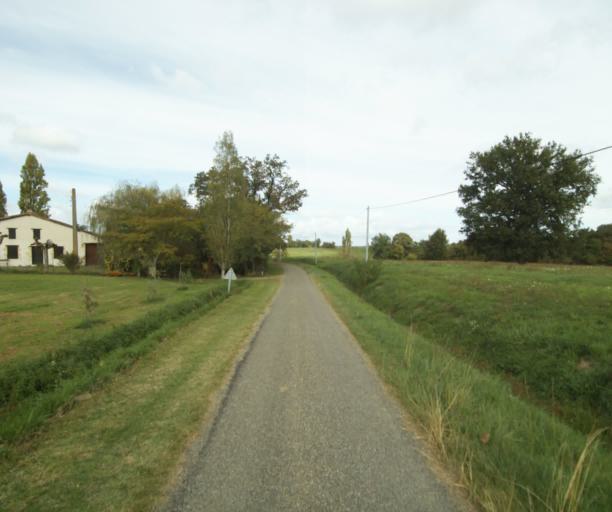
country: FR
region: Midi-Pyrenees
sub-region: Departement du Gers
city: Eauze
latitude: 43.8377
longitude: 0.1185
